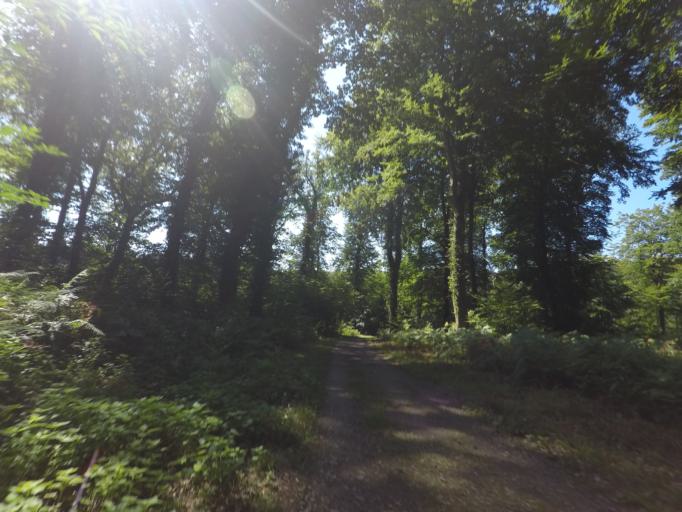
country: LU
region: Luxembourg
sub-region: Canton de Luxembourg
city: Strassen
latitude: 49.6386
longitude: 6.0759
